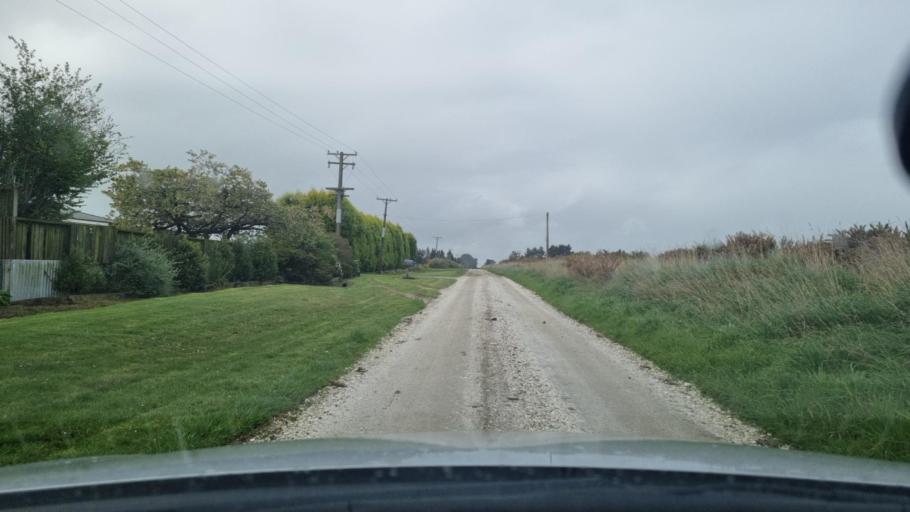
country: NZ
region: Southland
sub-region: Invercargill City
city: Invercargill
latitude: -46.4958
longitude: 168.4199
